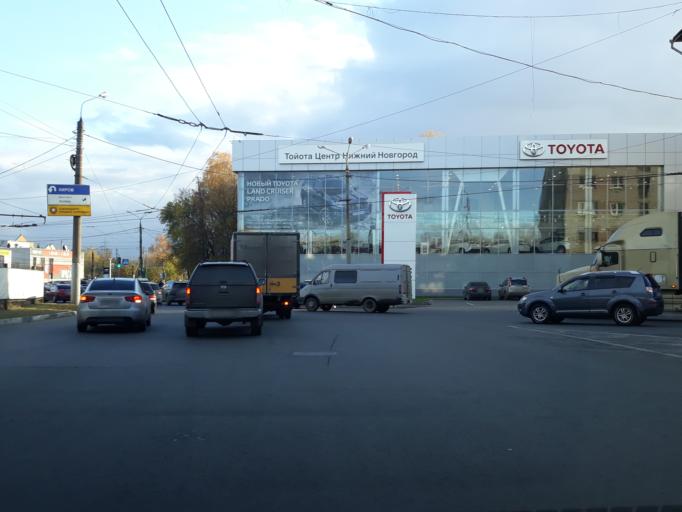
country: RU
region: Nizjnij Novgorod
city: Nizhniy Novgorod
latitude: 56.3147
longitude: 43.8982
